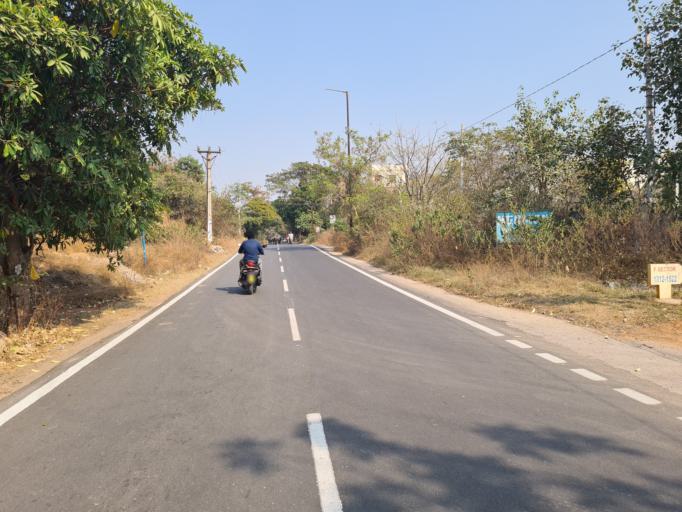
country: IN
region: Telangana
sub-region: Medak
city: Serilingampalle
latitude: 17.4848
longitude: 78.3019
